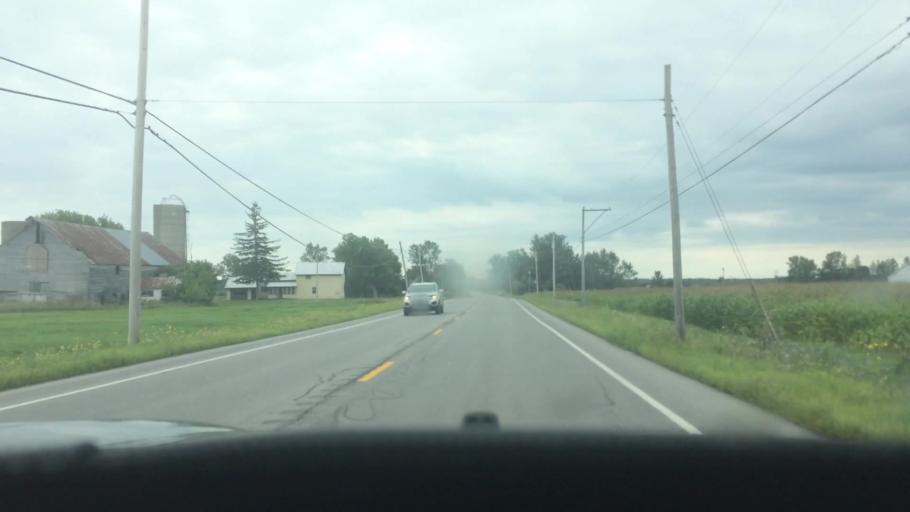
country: US
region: New York
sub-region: St. Lawrence County
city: Ogdensburg
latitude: 44.6732
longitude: -75.4735
